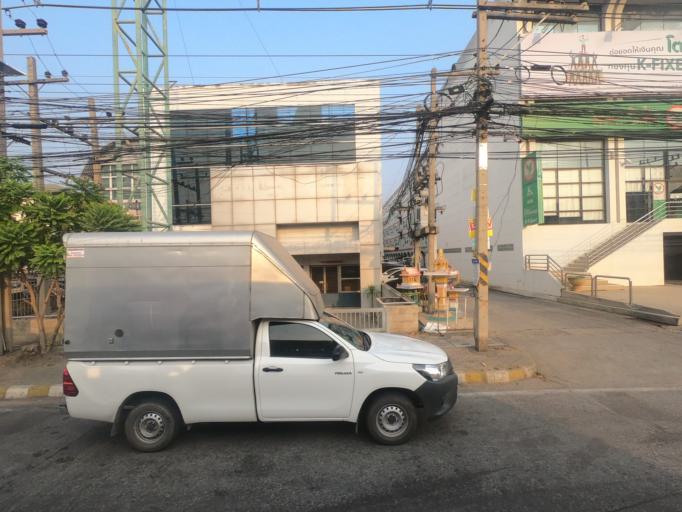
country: TH
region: Pathum Thani
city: Khlong Luang
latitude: 14.1471
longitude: 100.6187
